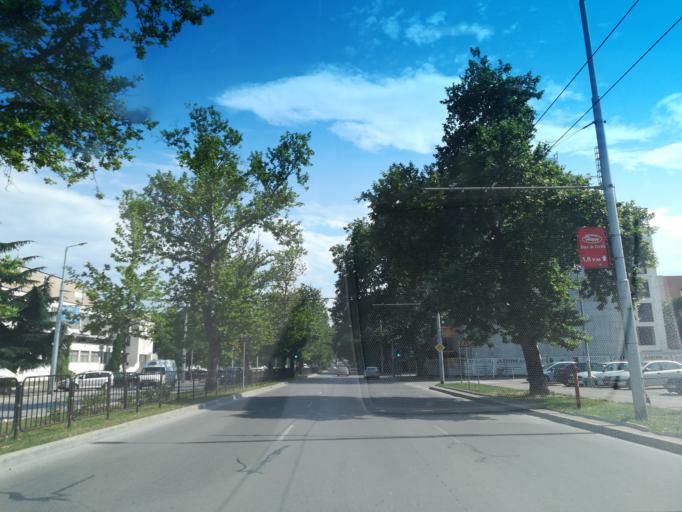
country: BG
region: Plovdiv
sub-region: Obshtina Plovdiv
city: Plovdiv
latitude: 42.1394
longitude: 24.7630
